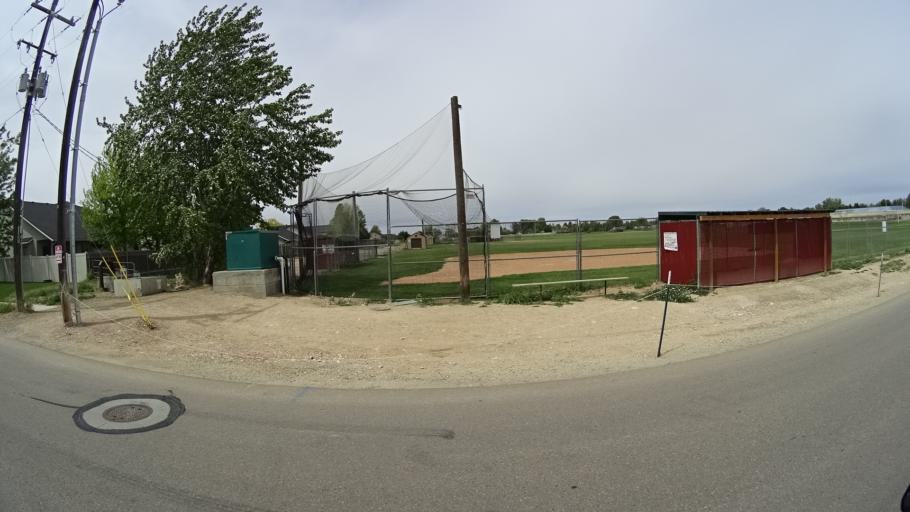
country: US
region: Idaho
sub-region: Ada County
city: Meridian
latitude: 43.5502
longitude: -116.3244
